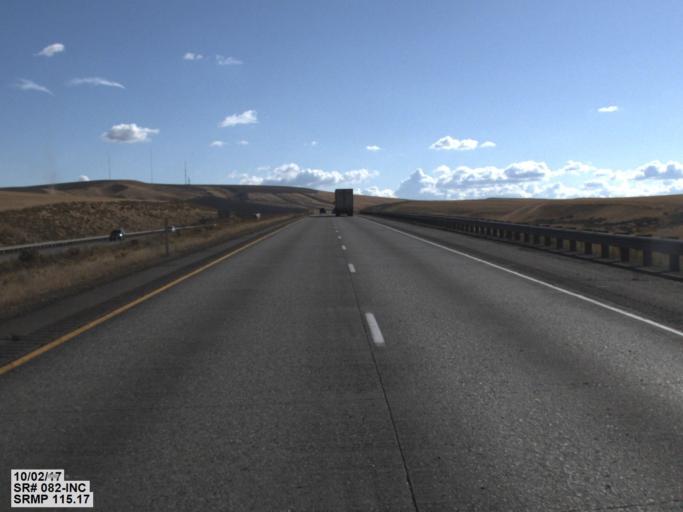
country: US
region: Washington
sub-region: Benton County
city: Highland
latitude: 46.1313
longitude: -119.2024
